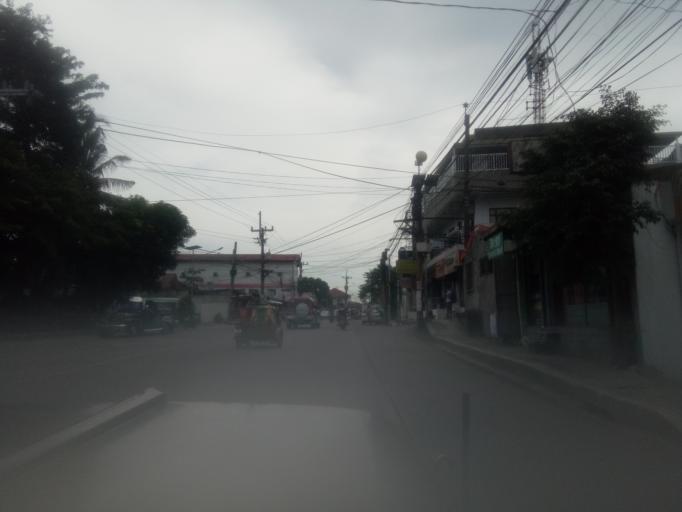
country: PH
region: Calabarzon
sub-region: Province of Cavite
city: Bulihan
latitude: 14.2909
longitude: 121.0044
